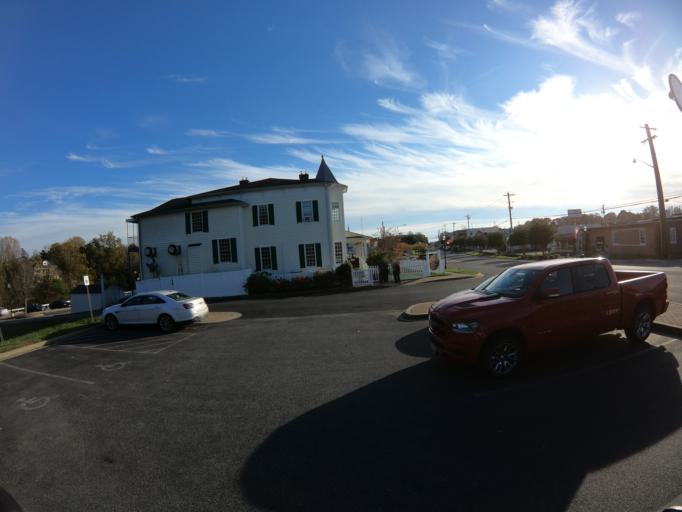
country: US
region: Maryland
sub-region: Saint Mary's County
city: Leonardtown
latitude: 38.2929
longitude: -76.6354
